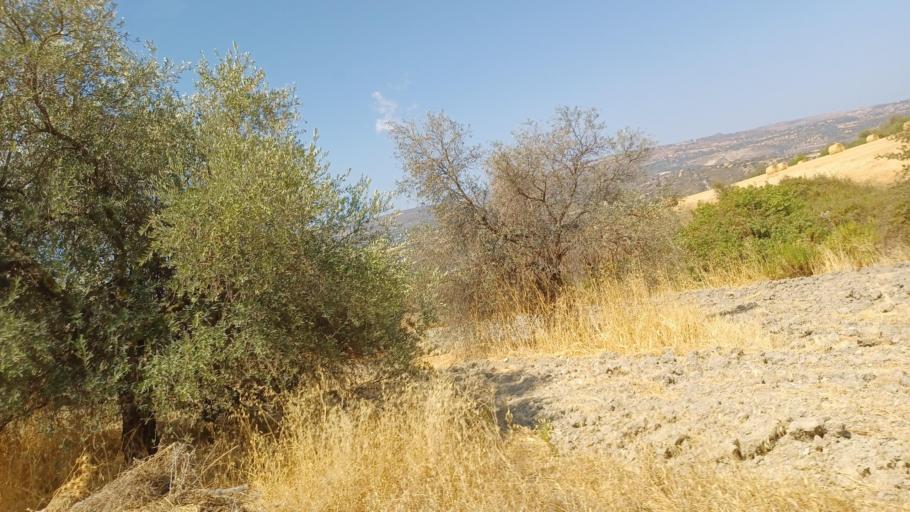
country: CY
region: Pafos
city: Polis
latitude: 34.9706
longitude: 32.4913
